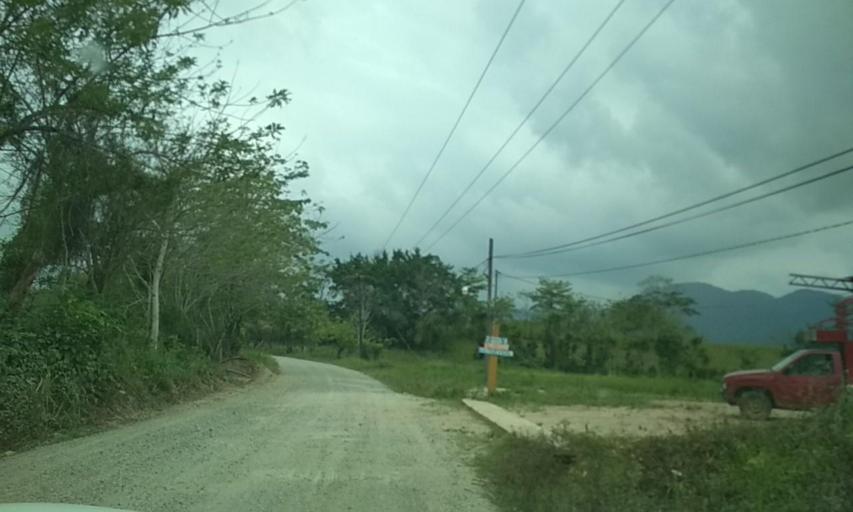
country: MX
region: Veracruz
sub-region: Uxpanapa
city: Poblado 10
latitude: 17.5004
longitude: -94.1481
